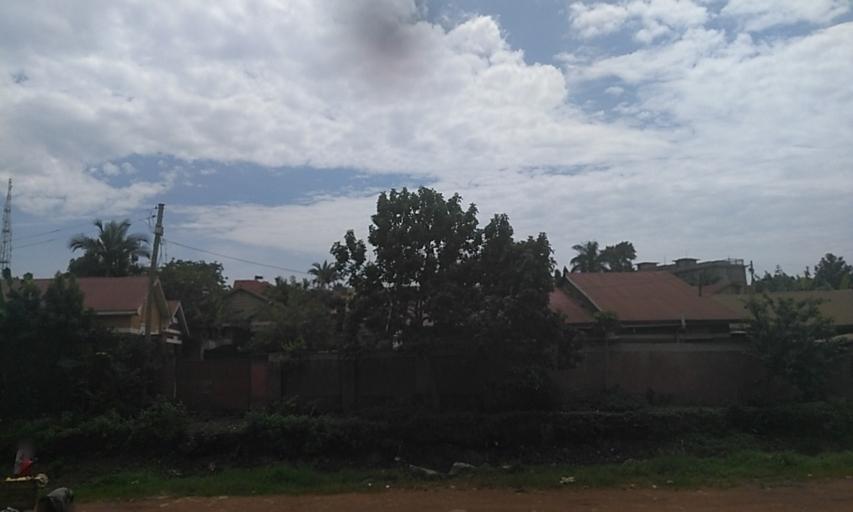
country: UG
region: Central Region
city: Kampala Central Division
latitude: 0.3580
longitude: 32.5934
